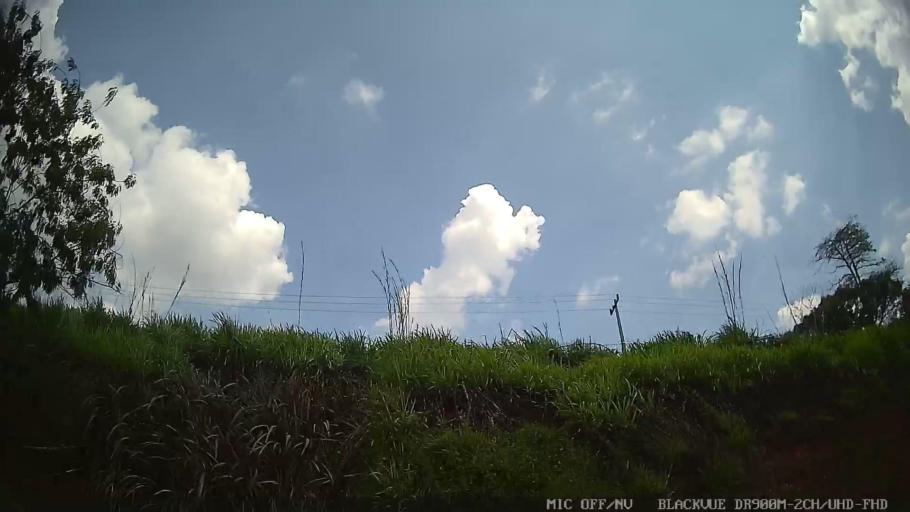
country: BR
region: Sao Paulo
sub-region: Itatiba
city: Itatiba
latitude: -22.9624
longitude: -46.7129
